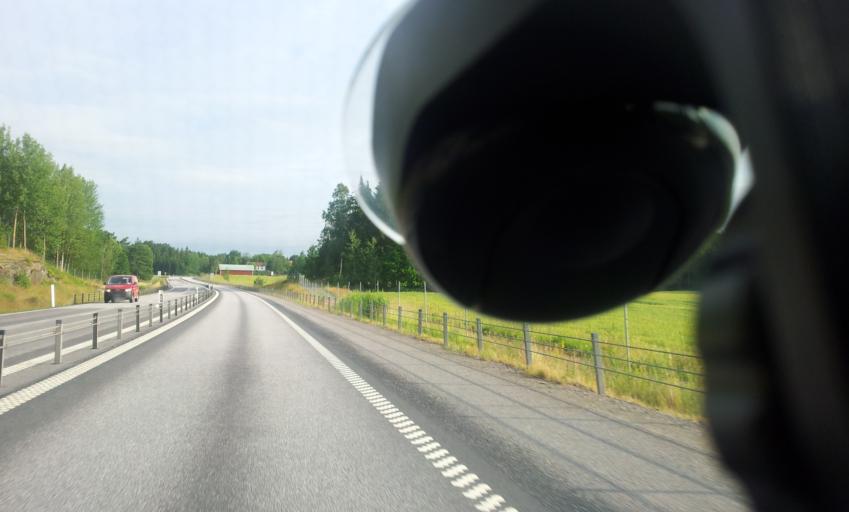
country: SE
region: OEstergoetland
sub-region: Valdemarsviks Kommun
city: Gusum
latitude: 58.3020
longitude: 16.4919
